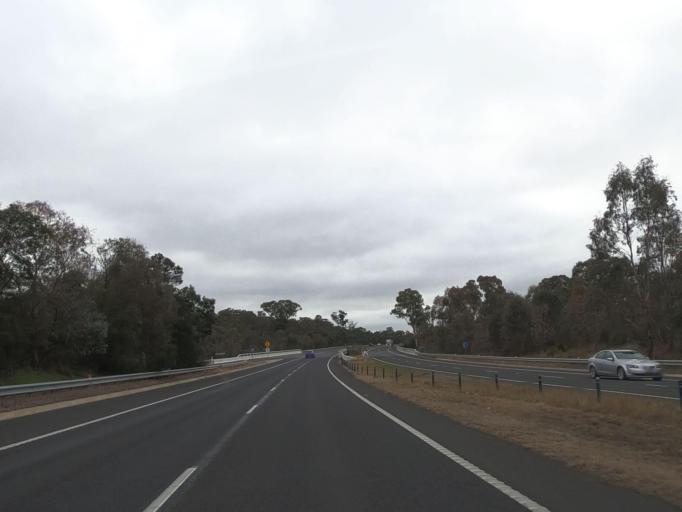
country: AU
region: Victoria
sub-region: Mount Alexander
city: Castlemaine
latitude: -37.0035
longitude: 144.2491
